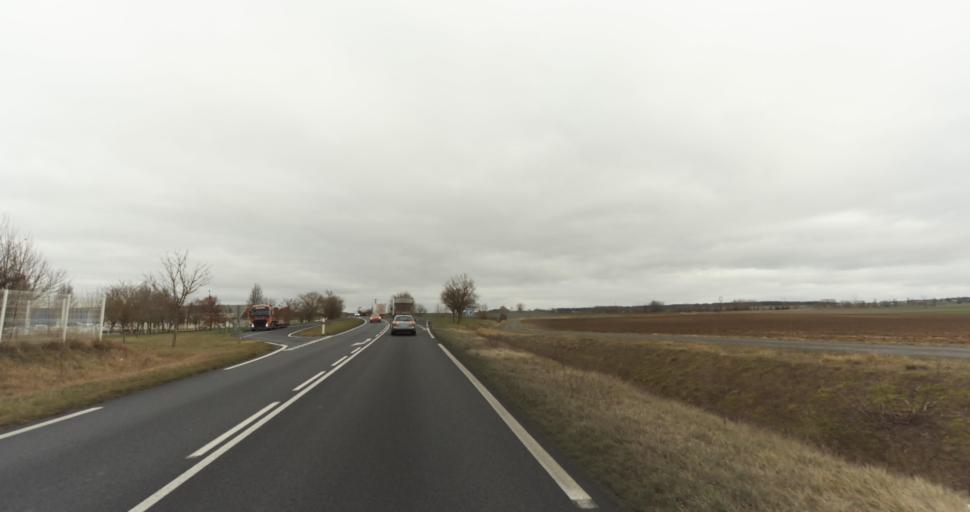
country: FR
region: Pays de la Loire
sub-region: Departement de Maine-et-Loire
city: Doue-la-Fontaine
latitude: 47.1878
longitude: -0.2433
